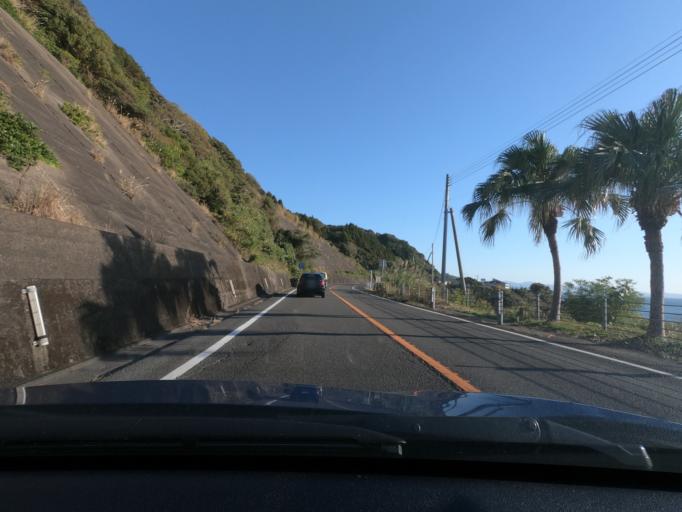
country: JP
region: Kagoshima
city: Akune
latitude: 31.9606
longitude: 130.2135
